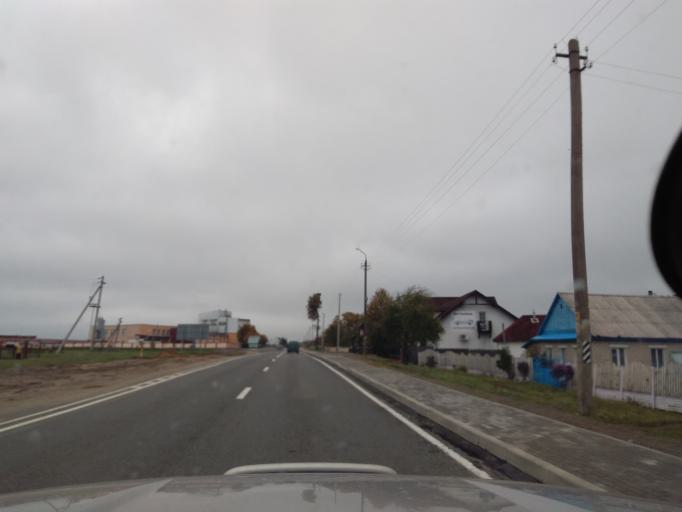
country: BY
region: Minsk
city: Kapyl'
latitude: 53.1402
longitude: 27.0892
